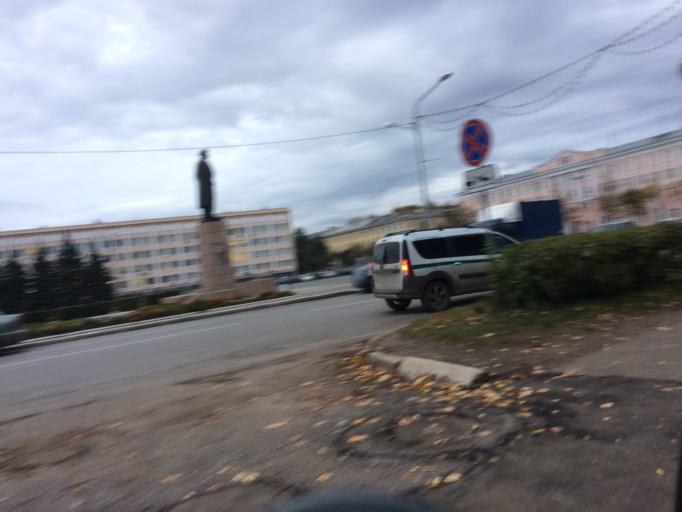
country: RU
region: Mariy-El
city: Yoshkar-Ola
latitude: 56.6314
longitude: 47.8899
